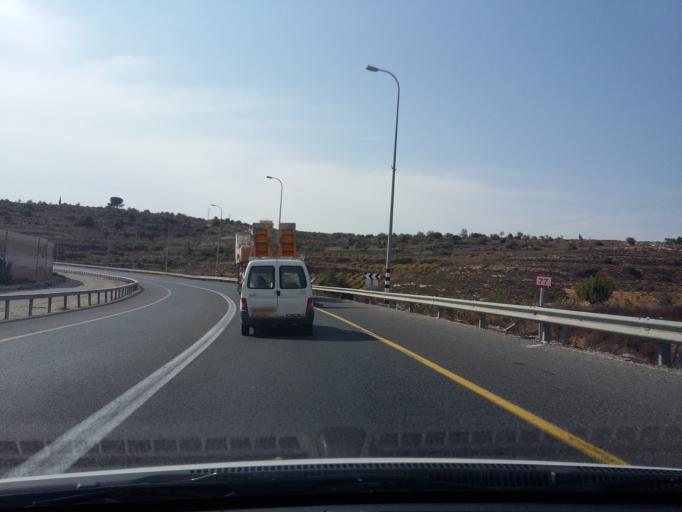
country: PS
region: West Bank
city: Al Khadir
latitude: 31.6963
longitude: 35.1553
